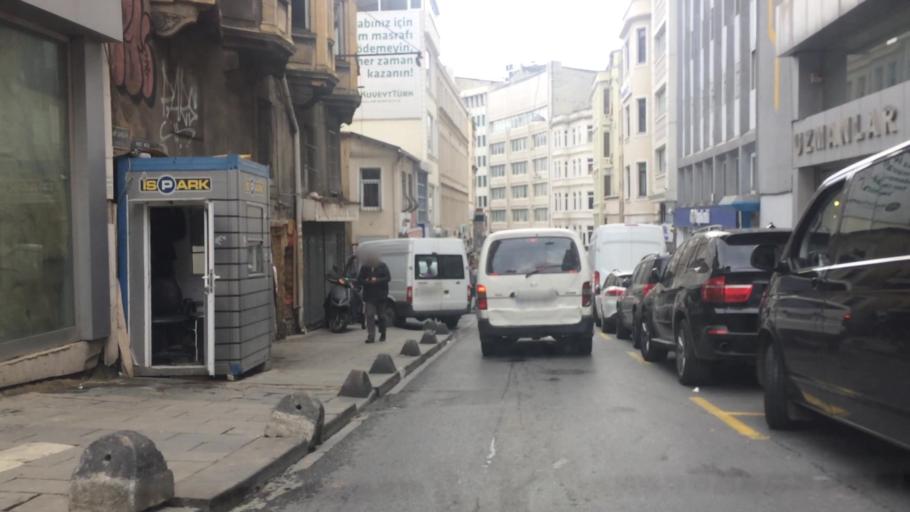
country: TR
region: Istanbul
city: Eminoenue
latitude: 41.0257
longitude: 28.9718
